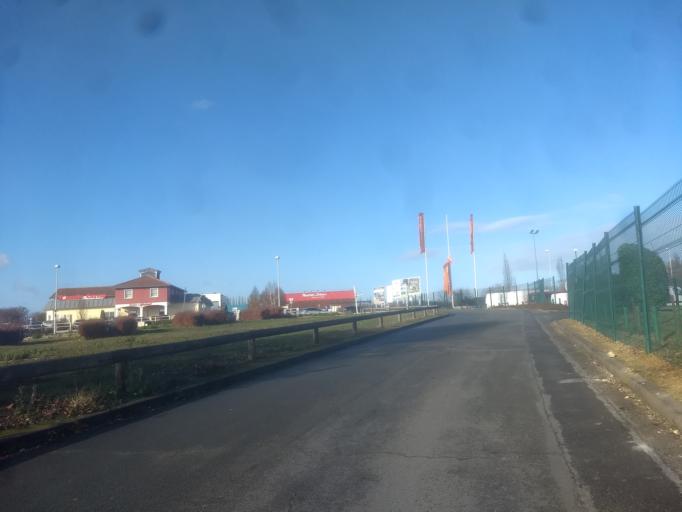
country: FR
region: Nord-Pas-de-Calais
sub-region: Departement du Pas-de-Calais
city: Anzin-Saint-Aubin
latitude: 50.3029
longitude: 2.7282
